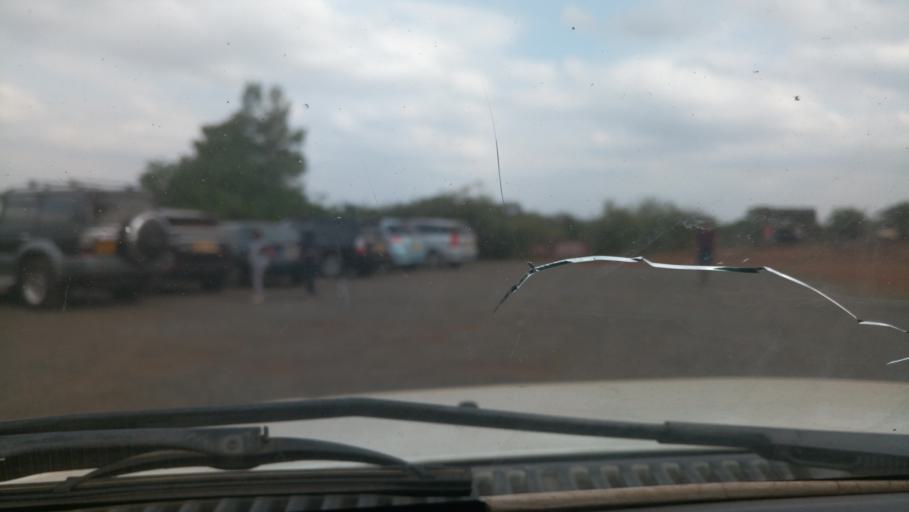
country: KE
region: Nairobi Area
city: Nairobi
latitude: -1.3577
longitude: 36.7942
